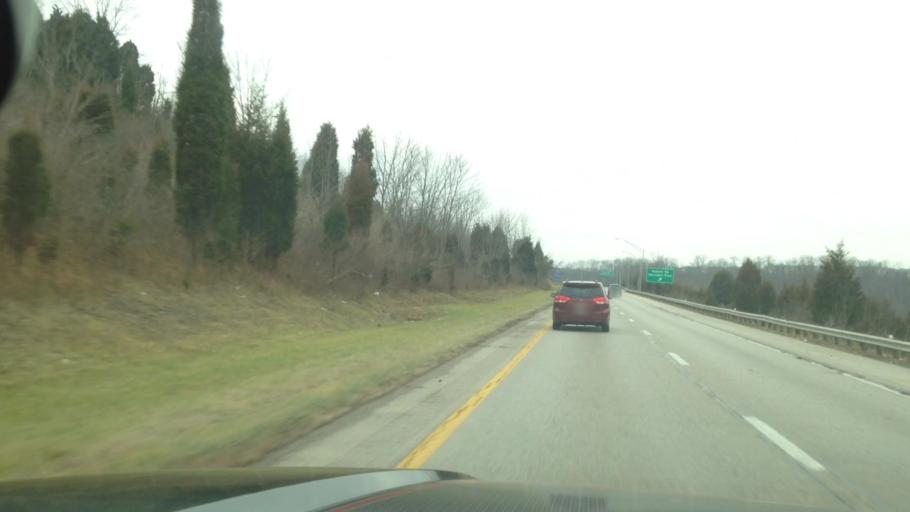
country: US
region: Ohio
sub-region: Hamilton County
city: Dent
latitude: 39.1962
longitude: -84.6541
